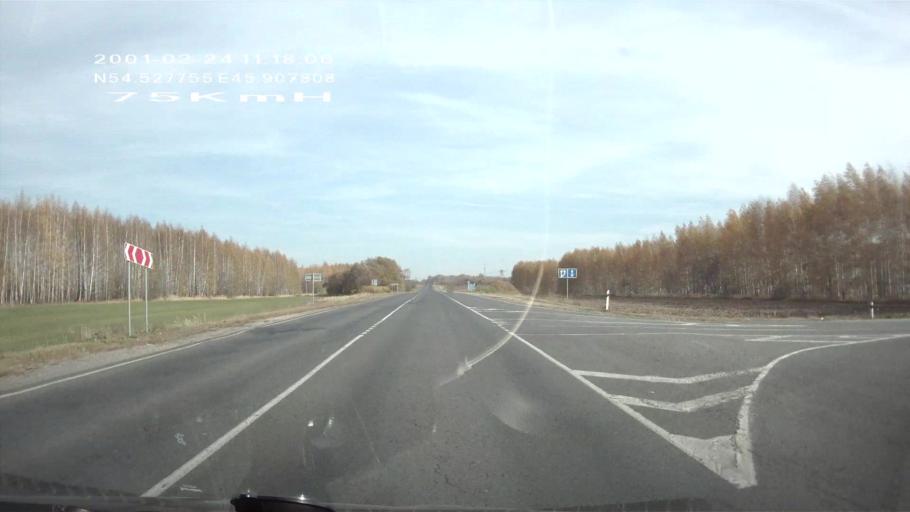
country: RU
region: Mordoviya
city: Atyashevo
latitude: 54.5276
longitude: 45.9076
